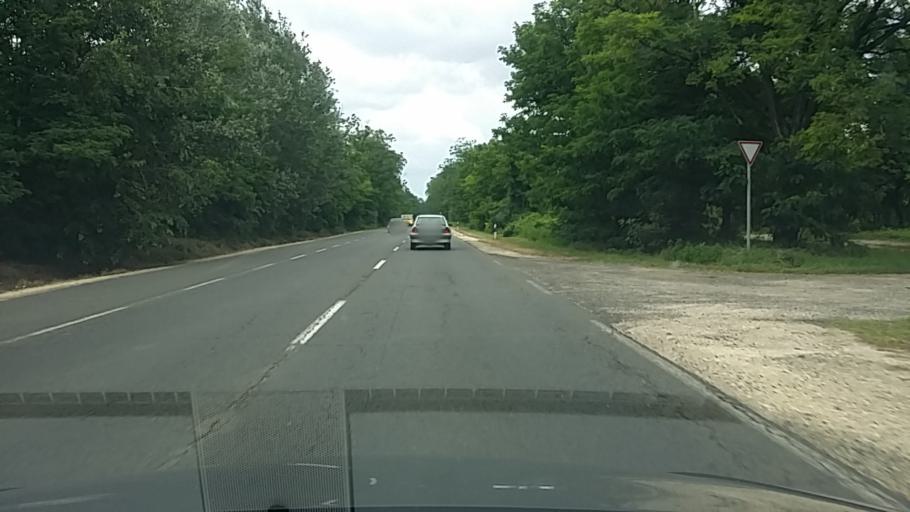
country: HU
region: Pest
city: Hernad
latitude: 47.1557
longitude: 19.3864
